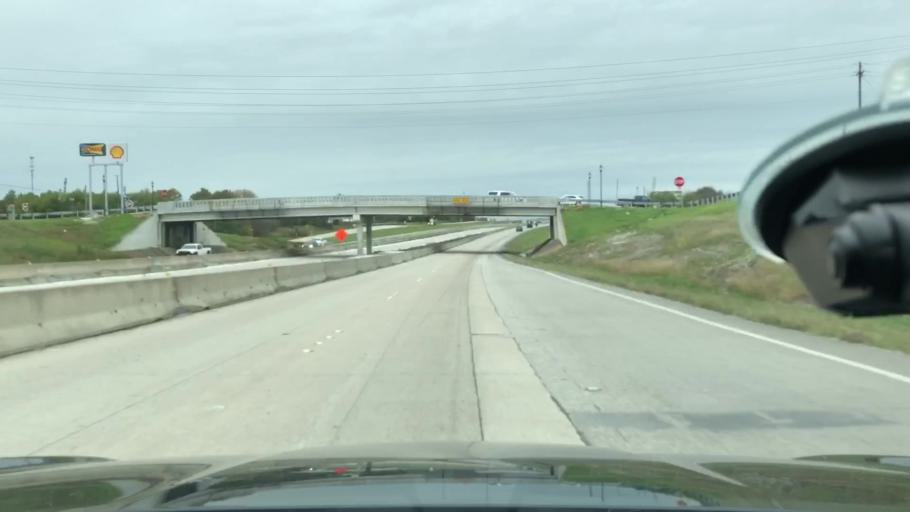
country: US
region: Texas
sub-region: Ellis County
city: Waxahachie
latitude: 32.3737
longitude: -96.8630
